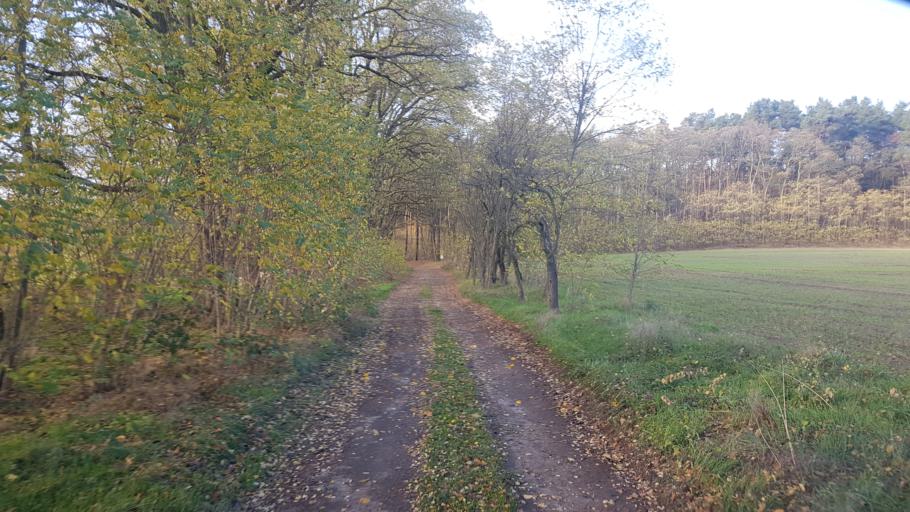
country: DE
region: Brandenburg
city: Calau
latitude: 51.6927
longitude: 13.9650
